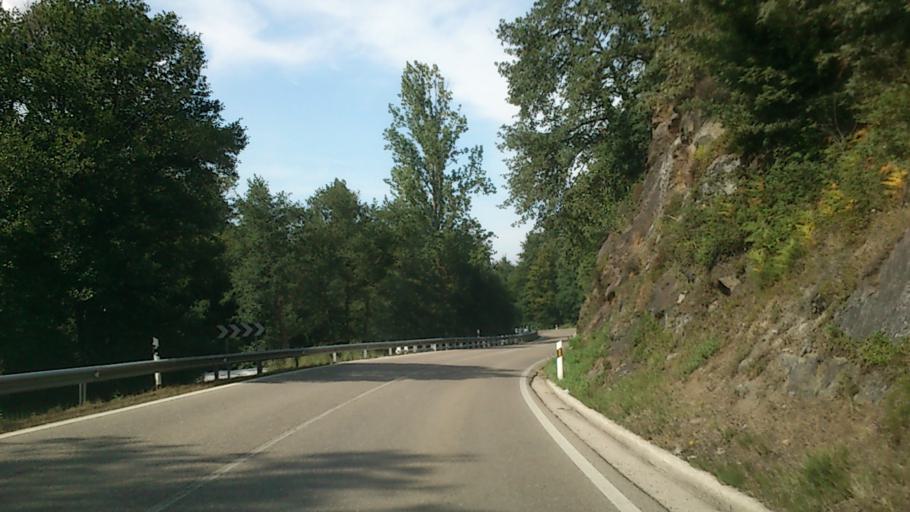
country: ES
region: Castille and Leon
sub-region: Provincia de Burgos
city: Espinosa de los Monteros
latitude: 43.0202
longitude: -3.4834
